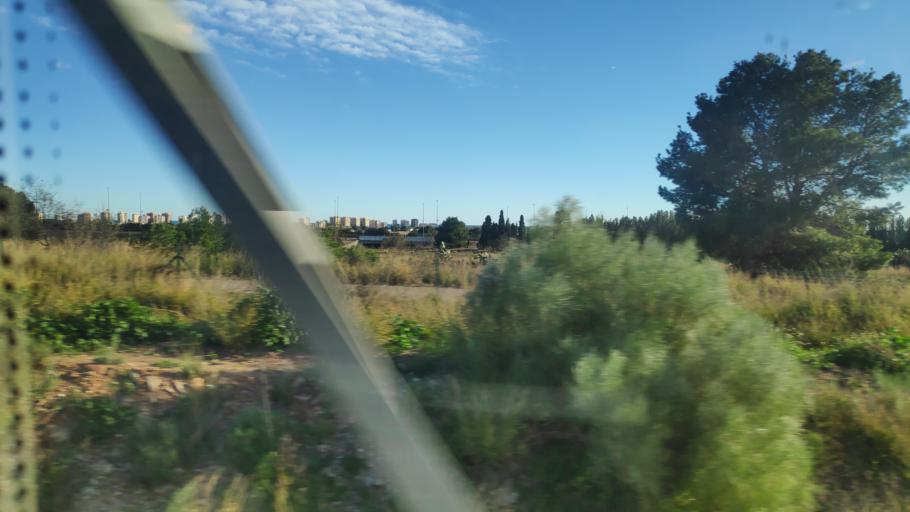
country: ES
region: Valencia
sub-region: Provincia de Castello
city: Benicassim
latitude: 40.0335
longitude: 0.0228
